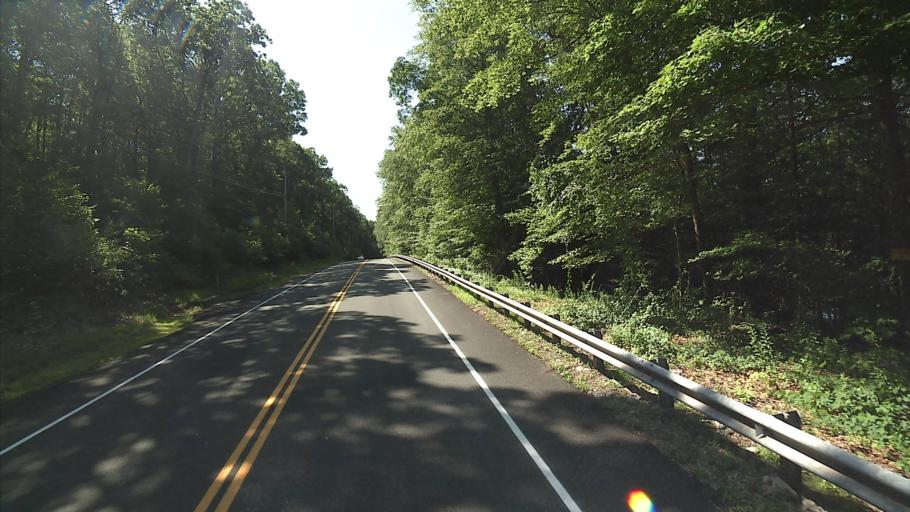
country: US
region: Connecticut
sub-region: Litchfield County
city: Northwest Harwinton
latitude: 41.7465
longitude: -73.0191
